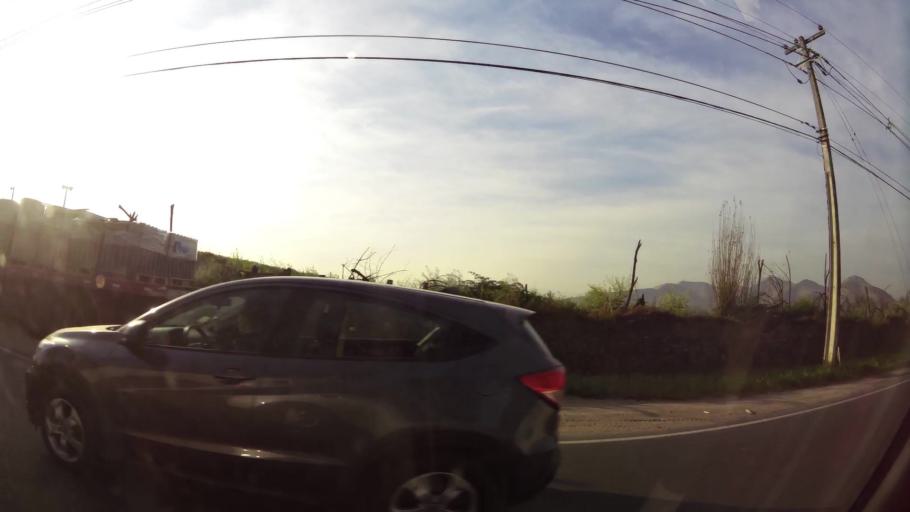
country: CL
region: Santiago Metropolitan
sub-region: Provincia de Maipo
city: San Bernardo
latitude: -33.5502
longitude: -70.7490
